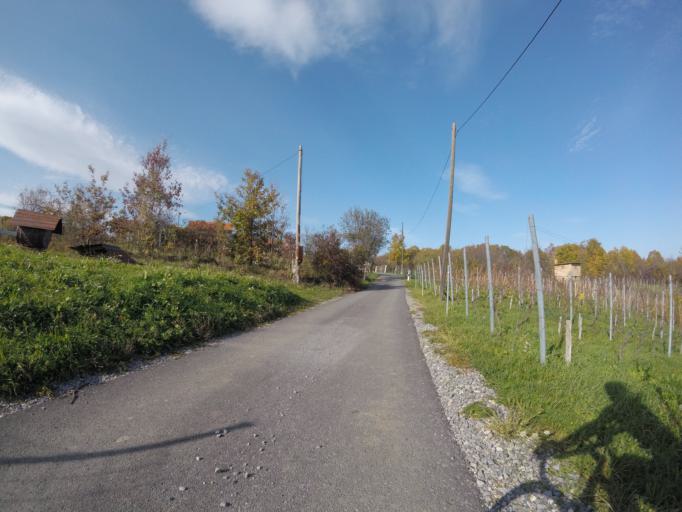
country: HR
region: Zagrebacka
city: Gradici
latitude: 45.6263
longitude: 16.0175
